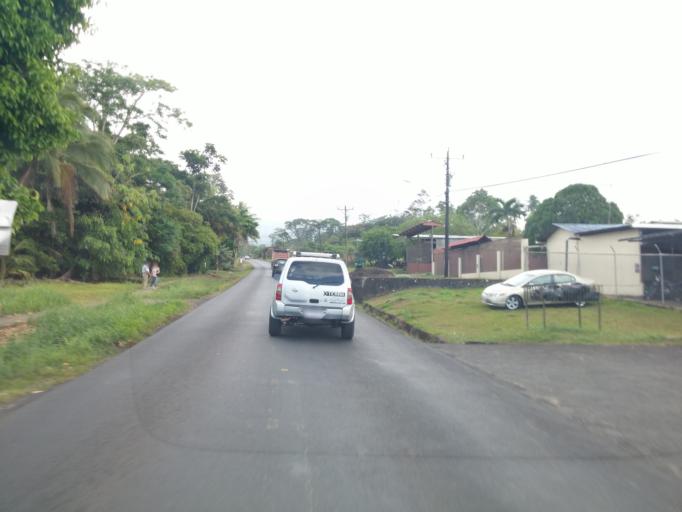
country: CR
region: Alajuela
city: Pital
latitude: 10.3963
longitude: -84.3380
